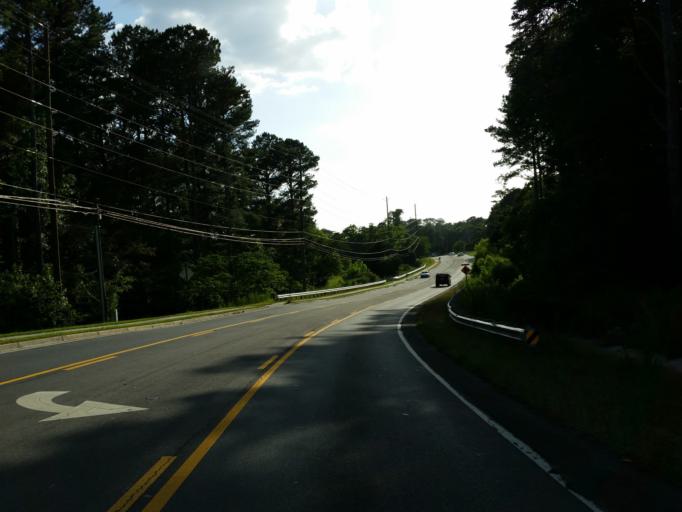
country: US
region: Georgia
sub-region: Cherokee County
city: Woodstock
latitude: 34.0705
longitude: -84.4928
